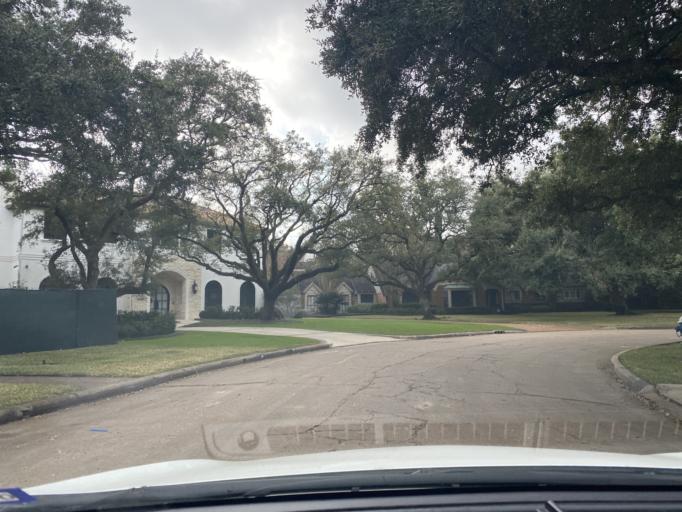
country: US
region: Texas
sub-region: Harris County
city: Hunters Creek Village
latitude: 29.7647
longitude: -95.4766
